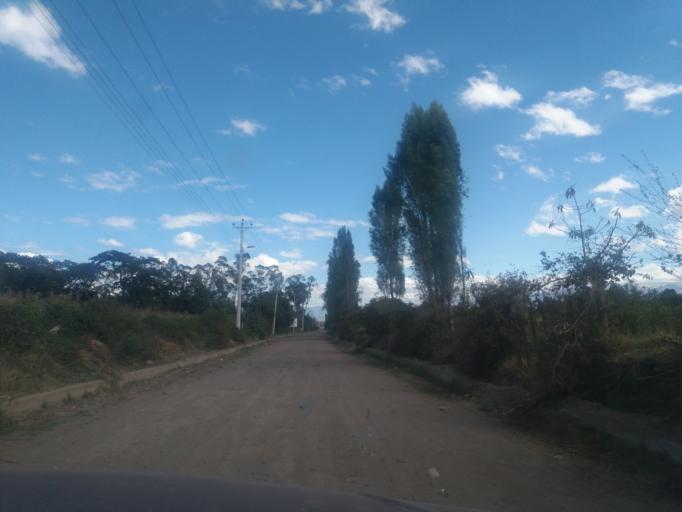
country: EC
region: Pichincha
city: Sangolqui
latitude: -0.1783
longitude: -78.3374
